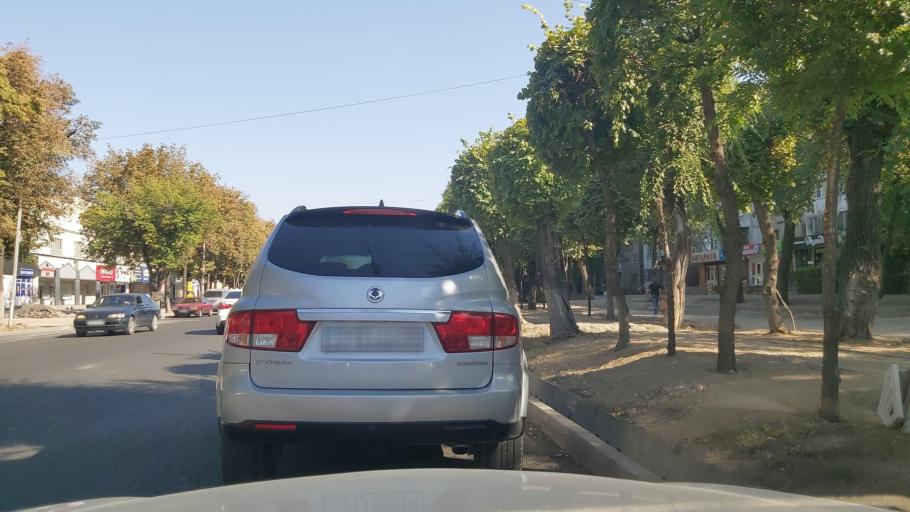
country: KZ
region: Almaty Oblysy
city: Pervomayskiy
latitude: 43.3225
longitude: 76.9126
